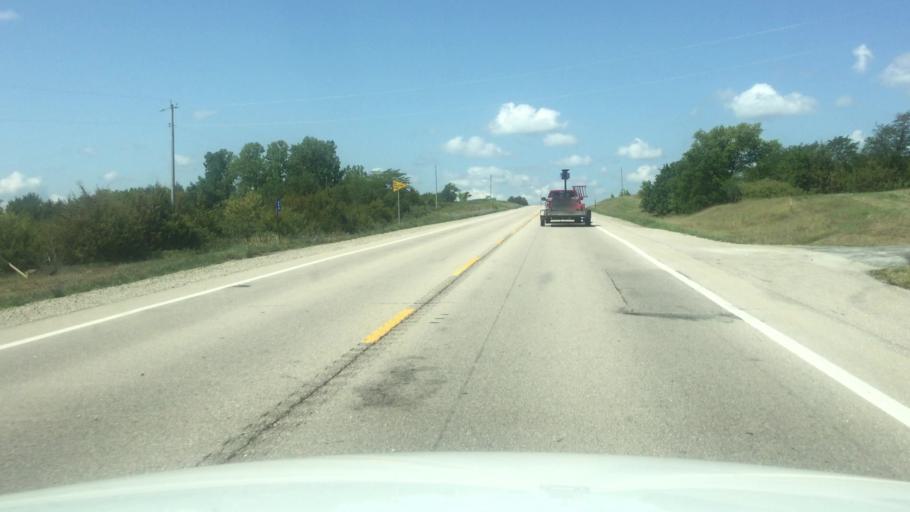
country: US
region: Kansas
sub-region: Nemaha County
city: Sabetha
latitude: 39.8430
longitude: -95.6867
